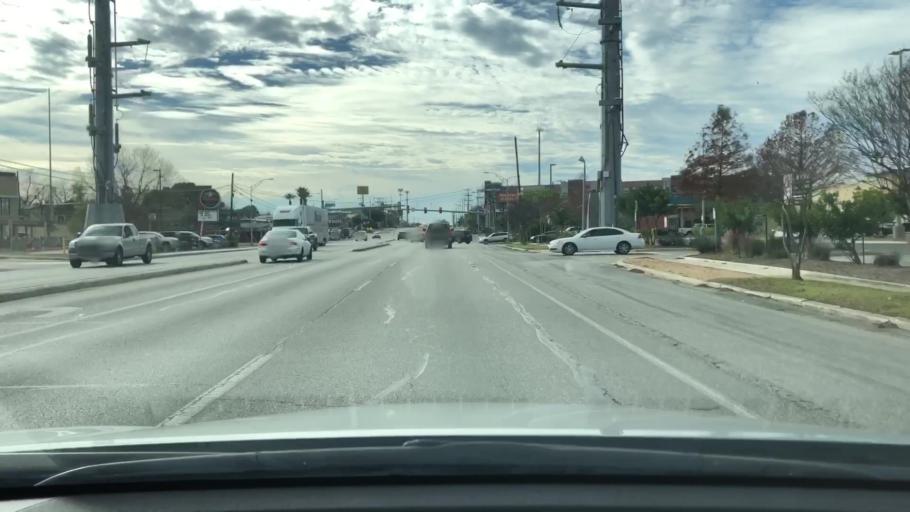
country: US
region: Texas
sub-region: Bexar County
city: Terrell Hills
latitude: 29.4881
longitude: -98.4460
